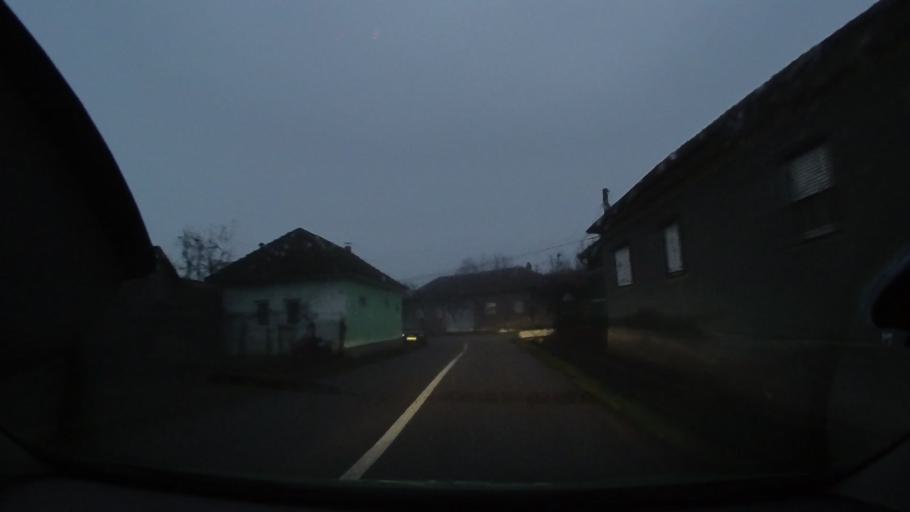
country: RO
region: Arad
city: Hatzmas
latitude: 46.5026
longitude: 22.0777
